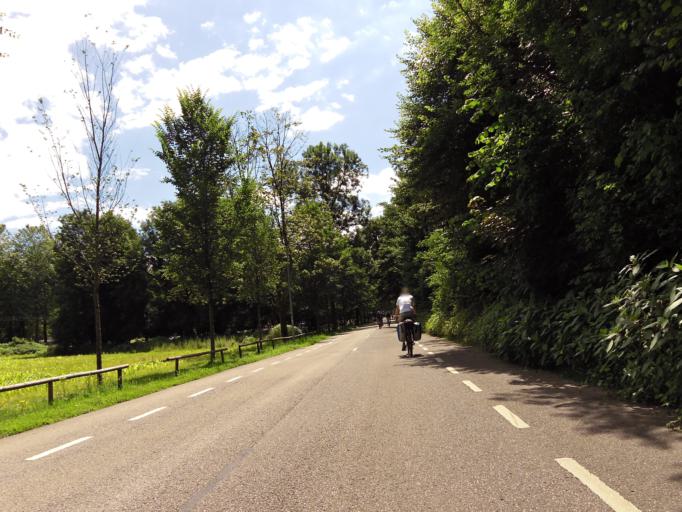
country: AT
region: Vorarlberg
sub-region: Politischer Bezirk Bregenz
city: Horbranz
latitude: 47.5433
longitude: 9.7258
